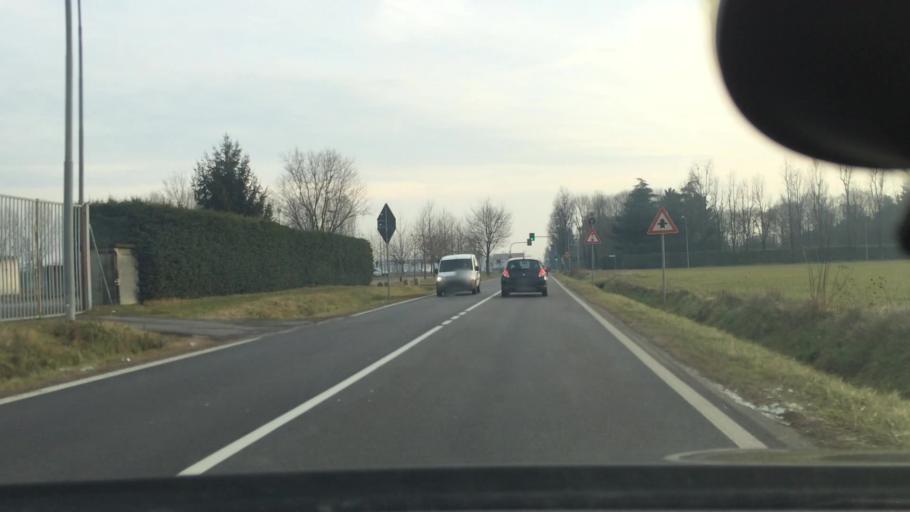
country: IT
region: Lombardy
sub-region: Provincia di Varese
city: Origgio
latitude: 45.6011
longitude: 9.0222
